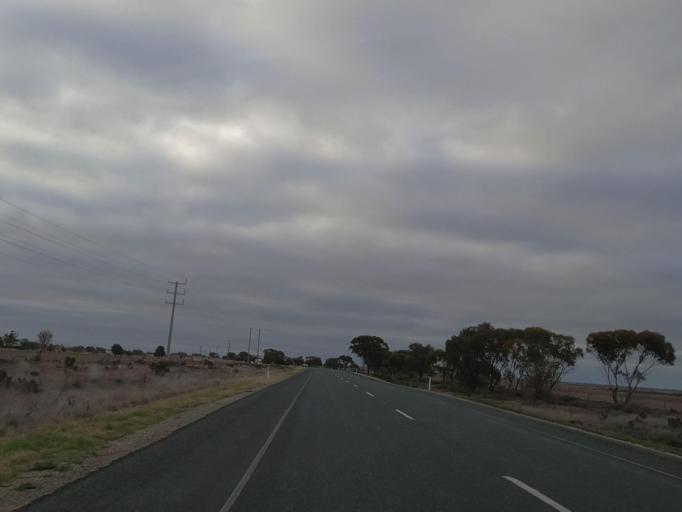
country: AU
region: Victoria
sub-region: Swan Hill
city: Swan Hill
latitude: -35.5864
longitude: 143.7903
